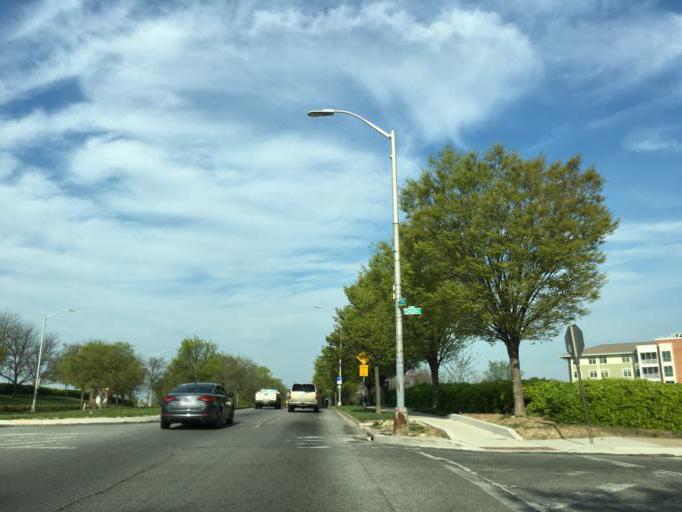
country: US
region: Maryland
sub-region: City of Baltimore
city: Baltimore
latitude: 39.3285
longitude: -76.5991
